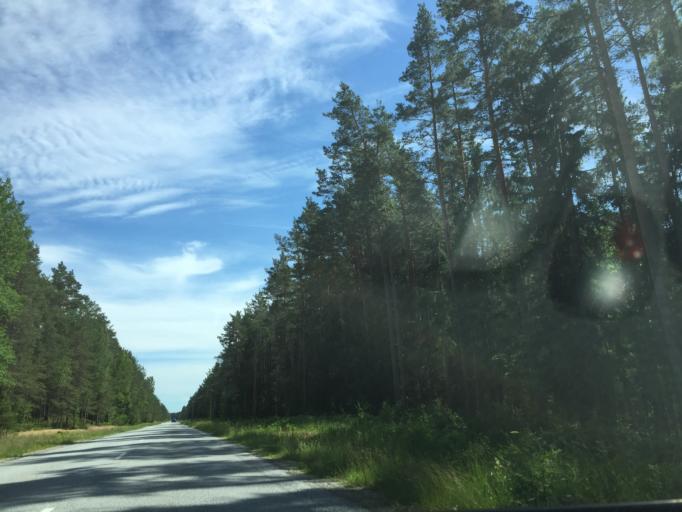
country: LV
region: Talsu Rajons
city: Valdemarpils
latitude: 57.6122
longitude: 22.5878
